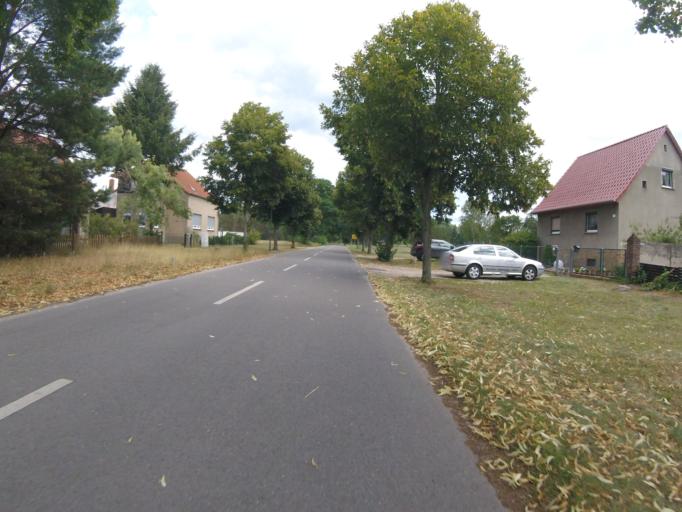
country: DE
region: Brandenburg
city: Gross Koris
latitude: 52.1473
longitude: 13.6895
